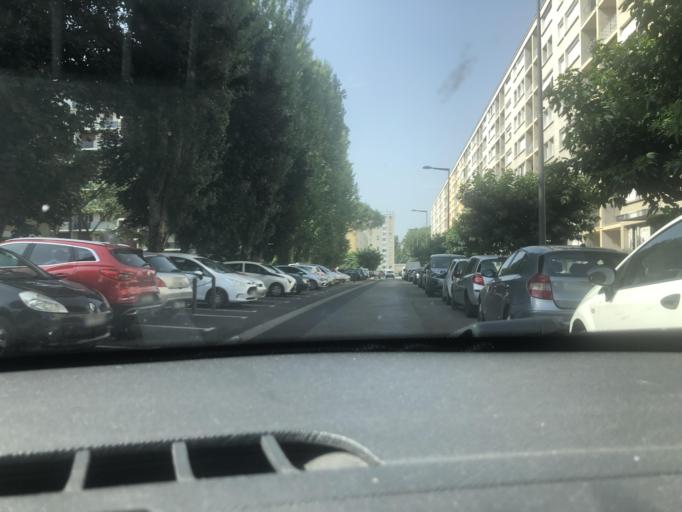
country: FR
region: Midi-Pyrenees
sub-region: Departement de la Haute-Garonne
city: Ramonville-Saint-Agne
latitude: 43.5760
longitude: 1.4621
